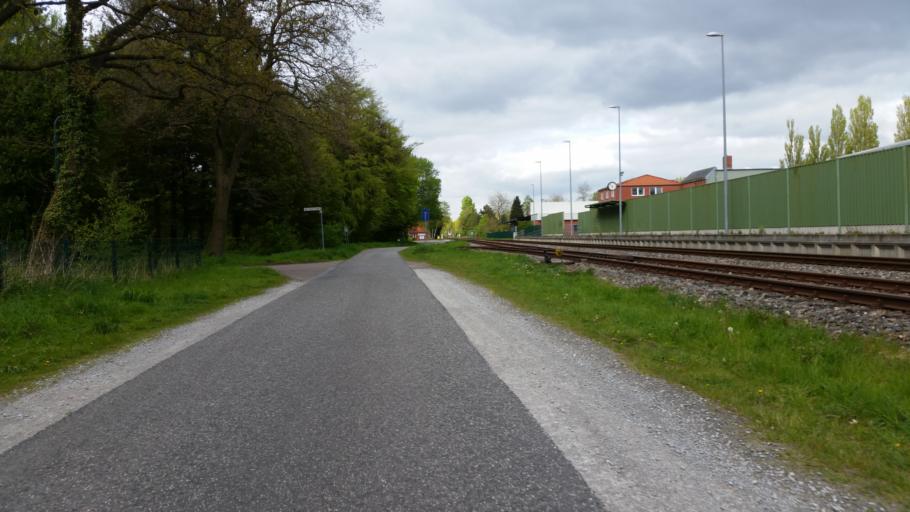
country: DE
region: Lower Saxony
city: Aurich
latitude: 53.4753
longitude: 7.4685
